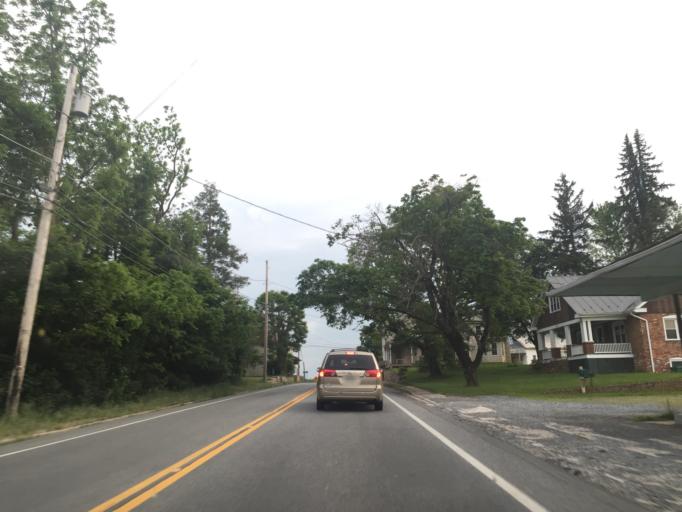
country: US
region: West Virginia
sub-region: Jefferson County
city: Charles Town
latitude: 39.2195
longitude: -77.9042
